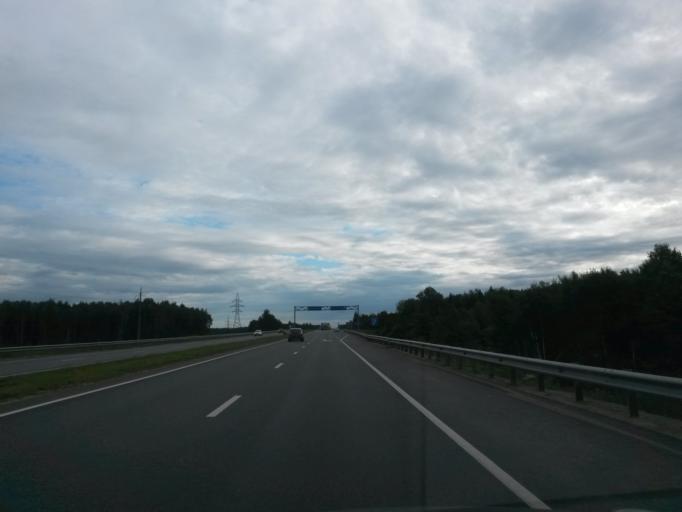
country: RU
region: Jaroslavl
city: Krasnyye Tkachi
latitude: 57.4010
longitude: 39.6495
